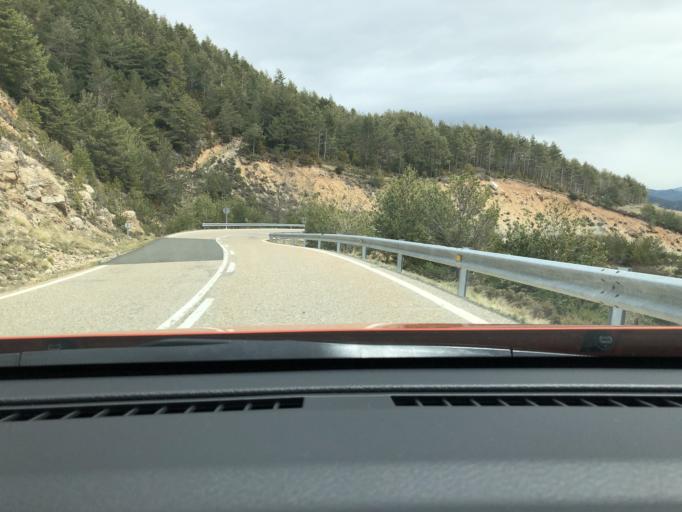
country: ES
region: Catalonia
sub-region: Provincia de Lleida
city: Olius
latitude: 42.1403
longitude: 1.5480
